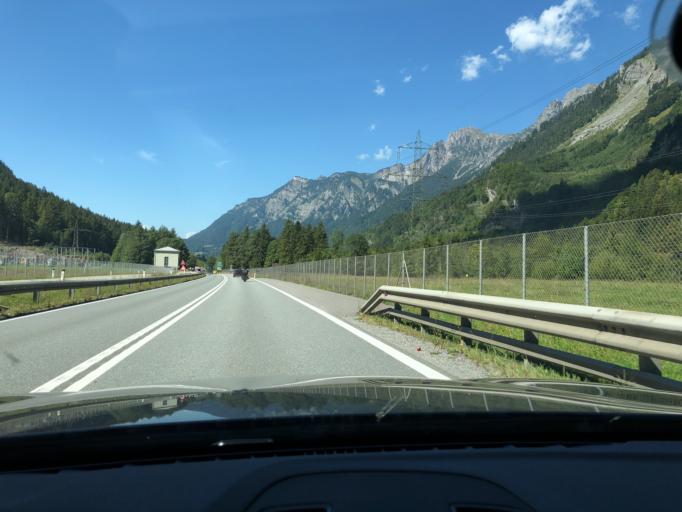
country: AT
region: Vorarlberg
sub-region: Politischer Bezirk Bludenz
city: Innerbraz
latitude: 47.1330
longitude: 9.9502
